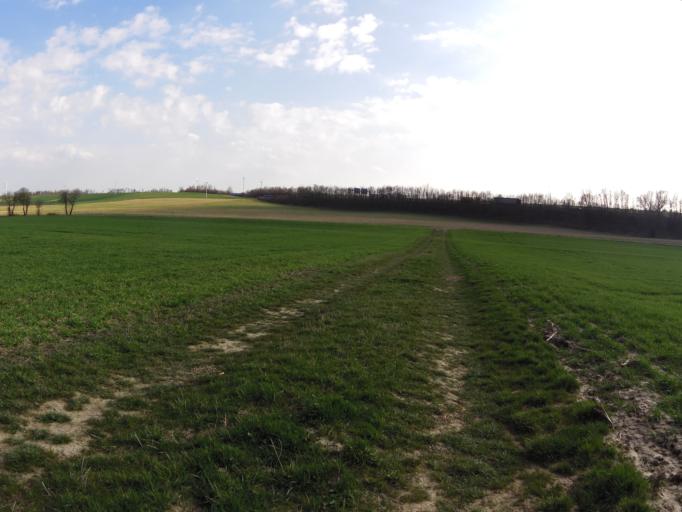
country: DE
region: Bavaria
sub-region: Regierungsbezirk Unterfranken
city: Biebelried
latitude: 49.7905
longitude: 10.0759
